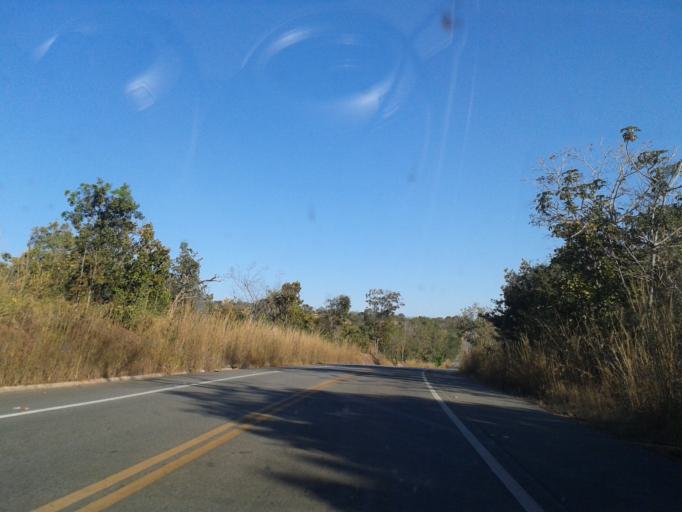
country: BR
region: Goias
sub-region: Itapuranga
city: Itapuranga
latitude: -15.6428
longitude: -50.2248
